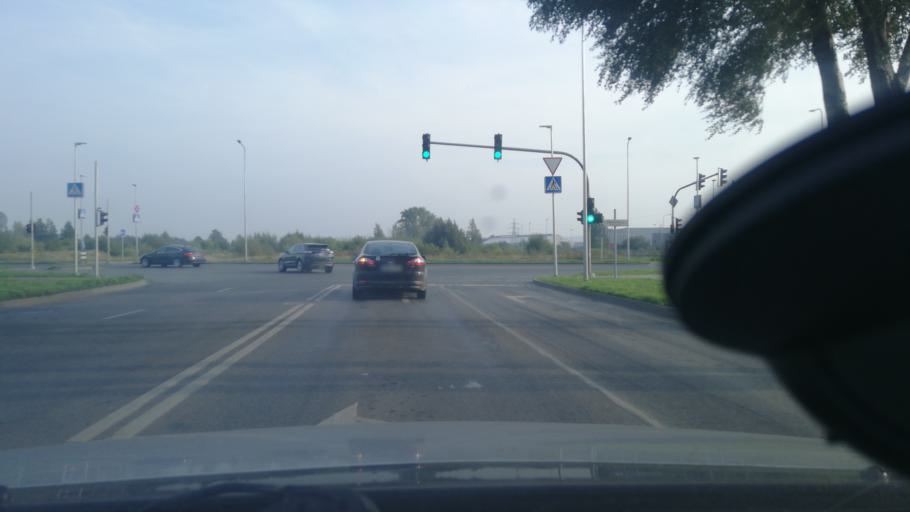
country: LT
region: Klaipedos apskritis
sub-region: Klaipeda
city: Klaipeda
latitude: 55.6554
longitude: 21.1718
